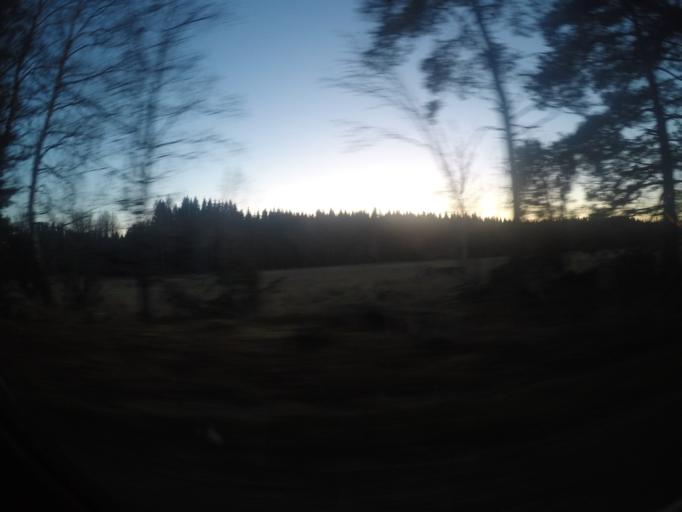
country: SE
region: OErebro
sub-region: Lindesbergs Kommun
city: Fellingsbro
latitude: 59.3577
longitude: 15.5821
